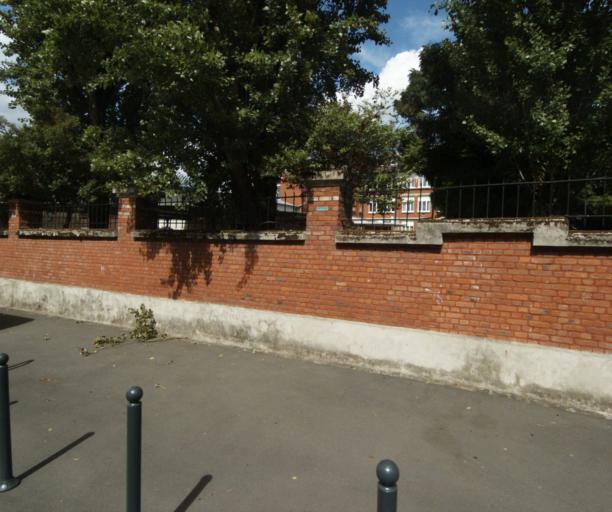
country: FR
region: Nord-Pas-de-Calais
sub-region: Departement du Nord
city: Roubaix
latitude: 50.6841
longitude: 3.1671
